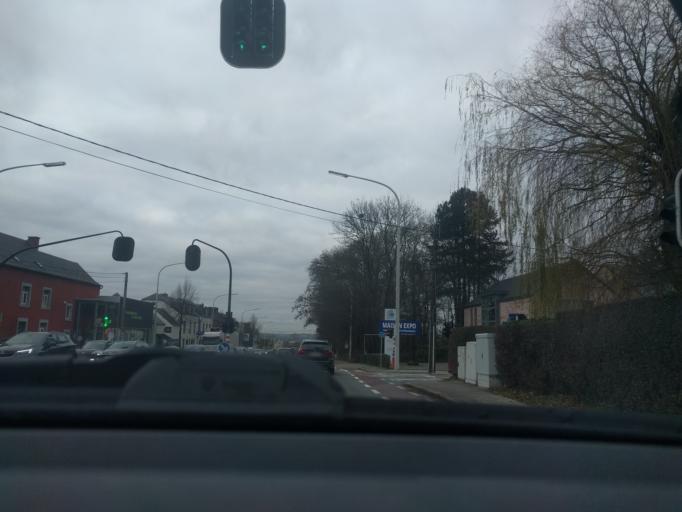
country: BE
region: Wallonia
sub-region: Province de Namur
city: Namur
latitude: 50.4436
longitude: 4.9026
